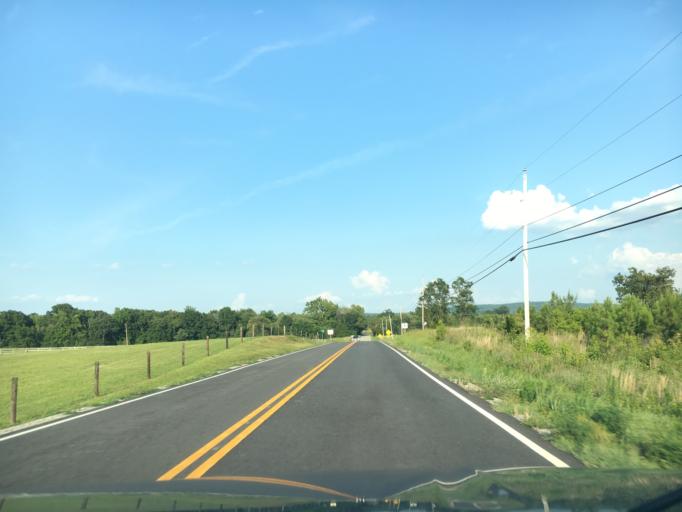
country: US
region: Virginia
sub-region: Pittsylvania County
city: Chatham
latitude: 36.8173
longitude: -79.3509
